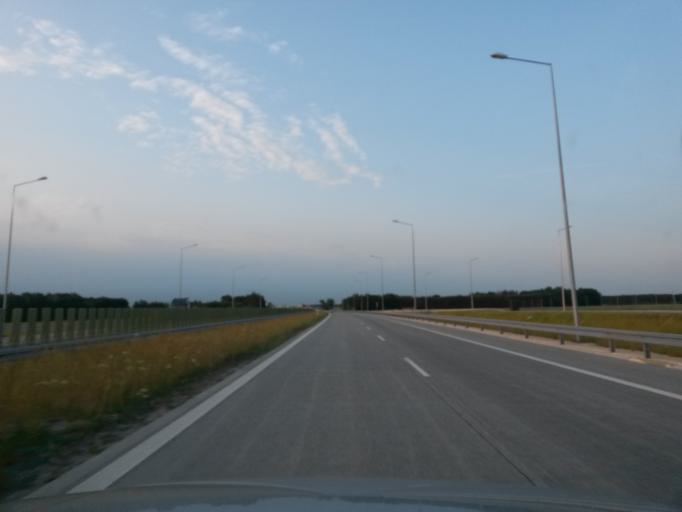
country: PL
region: Lodz Voivodeship
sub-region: Powiat wielunski
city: Czarnozyly
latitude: 51.3584
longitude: 18.5259
